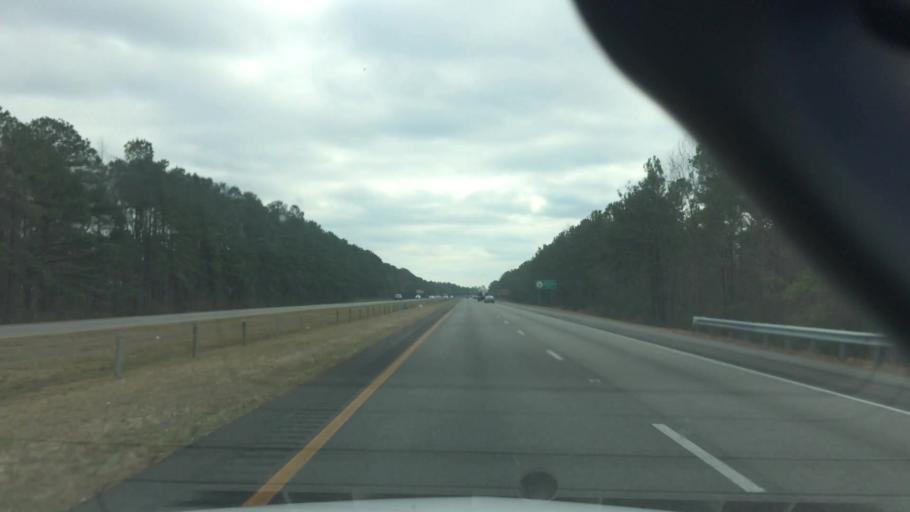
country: US
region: North Carolina
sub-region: New Hanover County
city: Skippers Corner
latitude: 34.3384
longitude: -77.8783
